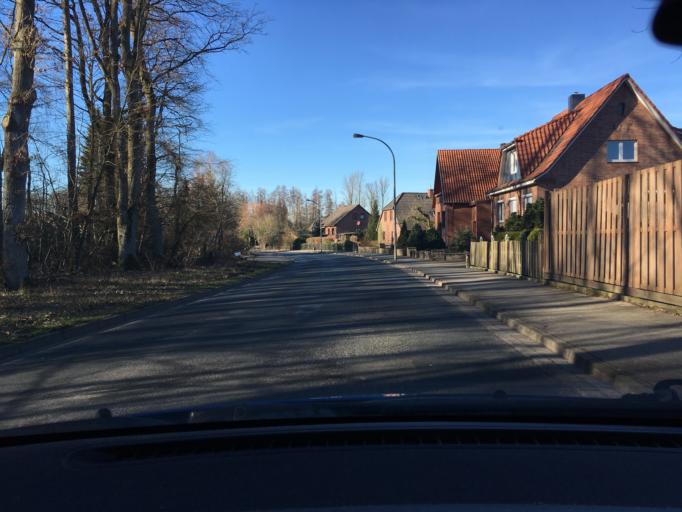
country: DE
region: Lower Saxony
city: Ebstorf
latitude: 53.0185
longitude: 10.4070
